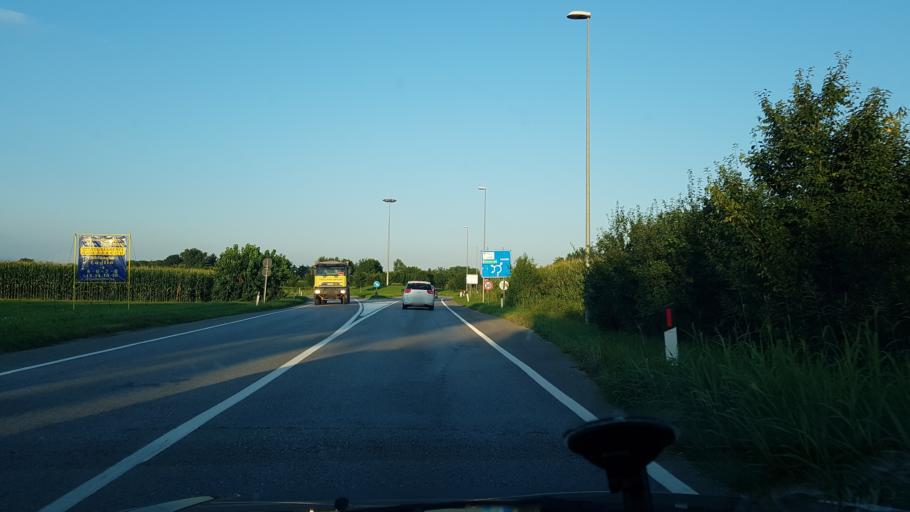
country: IT
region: Friuli Venezia Giulia
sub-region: Provincia di Udine
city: Martignacco
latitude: 46.0862
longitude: 13.1609
